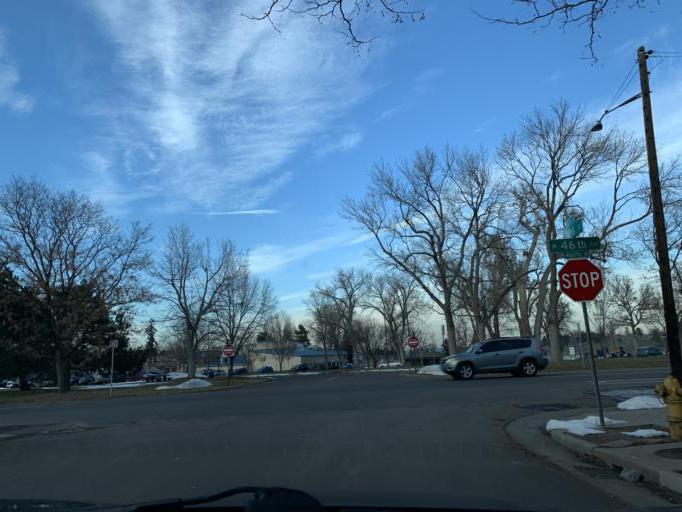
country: US
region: Colorado
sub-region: Jefferson County
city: Wheat Ridge
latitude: 39.7800
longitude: -105.0510
